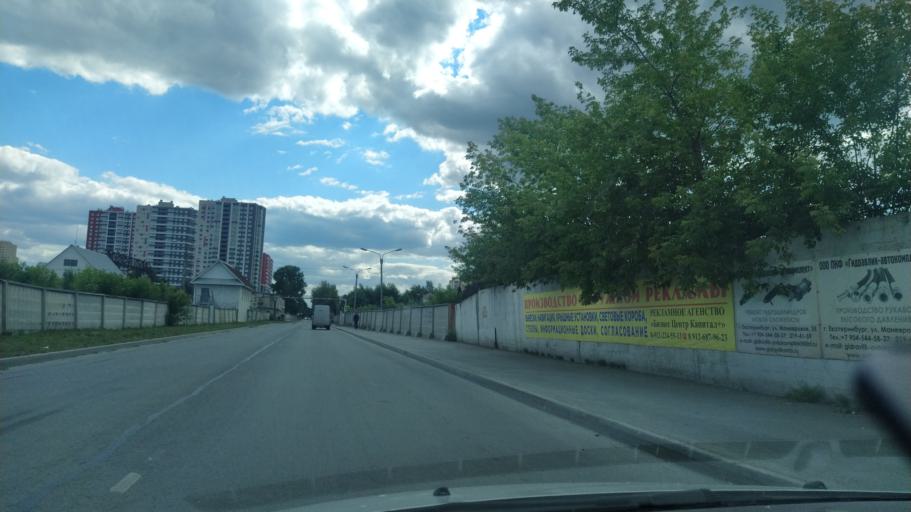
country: RU
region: Sverdlovsk
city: Shuvakish
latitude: 56.8814
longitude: 60.5281
